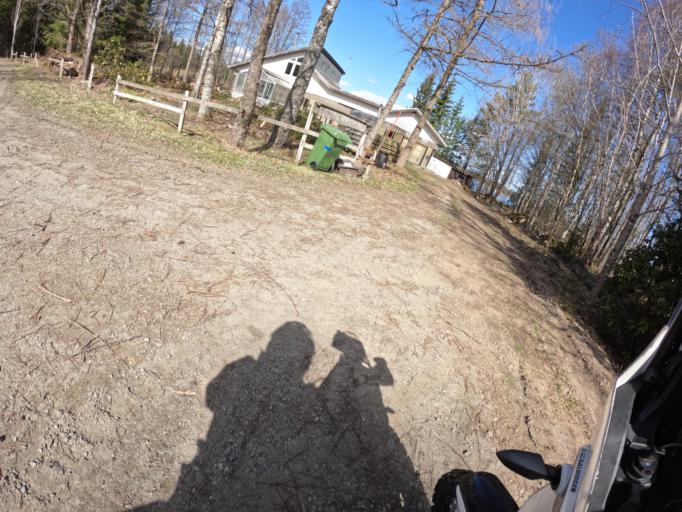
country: SE
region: Vaestra Goetaland
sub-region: Ulricehamns Kommun
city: Ulricehamn
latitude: 57.9341
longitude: 13.6130
